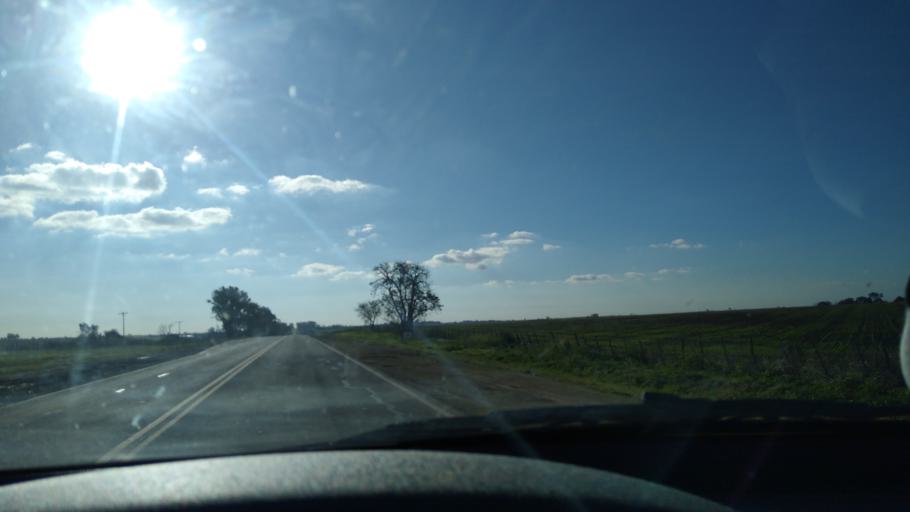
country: AR
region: Entre Rios
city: Diamante
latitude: -32.1230
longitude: -60.5655
